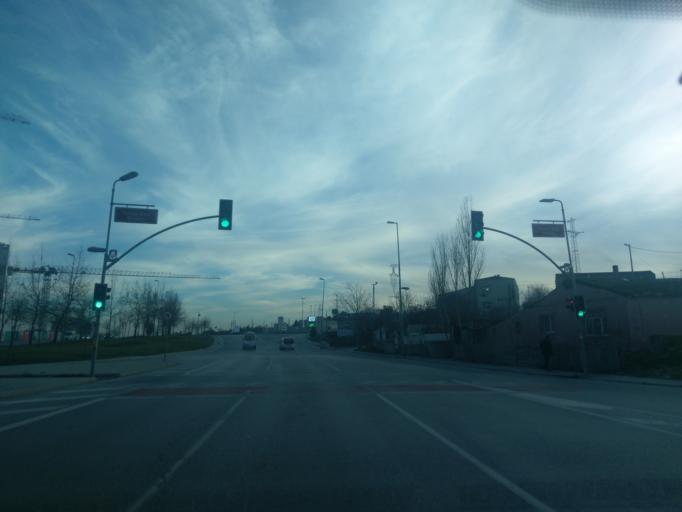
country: TR
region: Istanbul
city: Basaksehir
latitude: 41.0431
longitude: 28.7593
